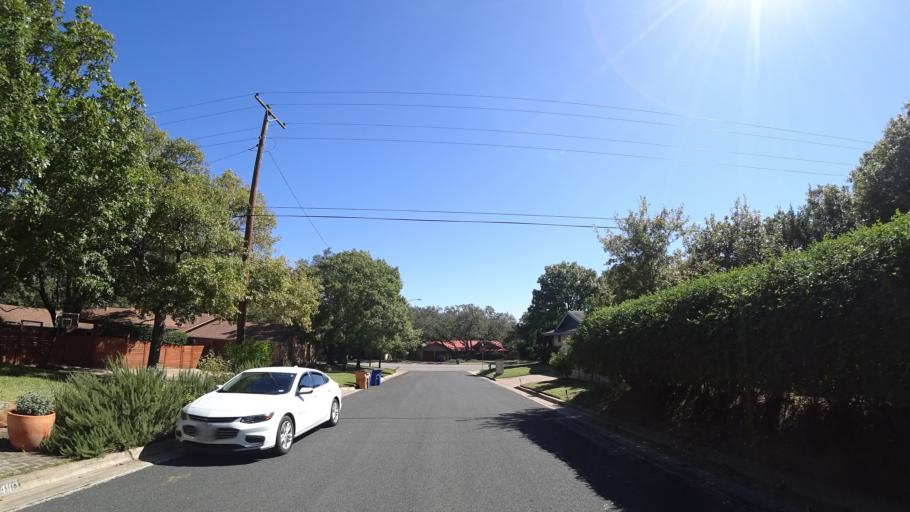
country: US
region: Texas
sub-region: Travis County
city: West Lake Hills
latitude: 30.3614
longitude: -97.7662
